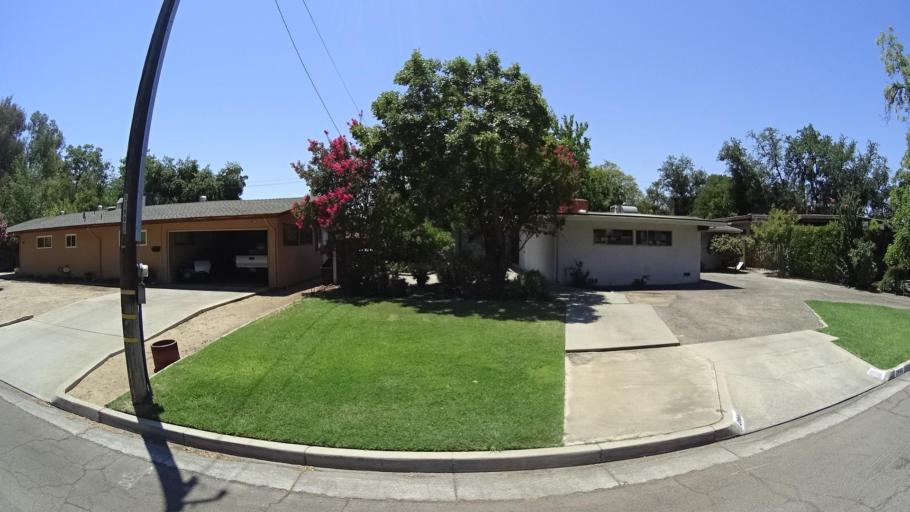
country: US
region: California
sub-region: Fresno County
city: Fresno
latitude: 36.7916
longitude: -119.7756
